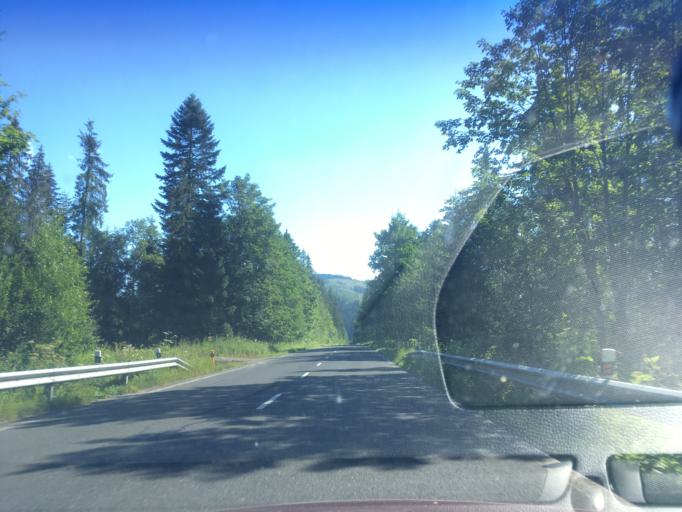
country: PL
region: Lesser Poland Voivodeship
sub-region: Powiat tatrzanski
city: Bukowina Tatrzanska
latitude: 49.2750
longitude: 20.1611
